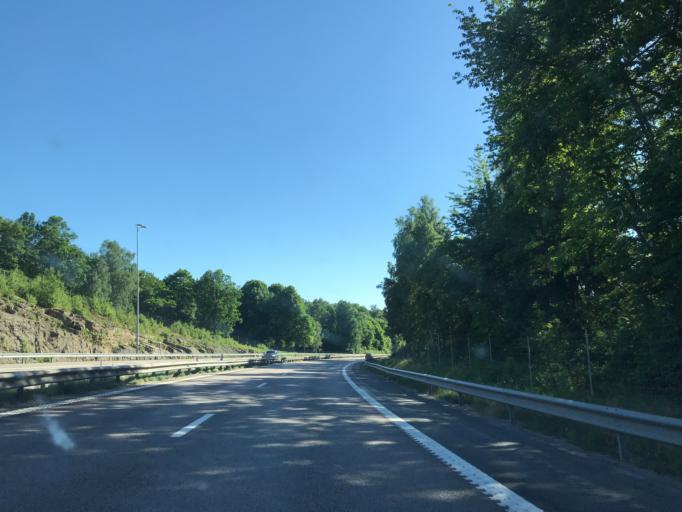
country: SE
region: Vaestra Goetaland
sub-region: Alingsas Kommun
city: Alingsas
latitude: 57.9051
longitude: 12.5014
